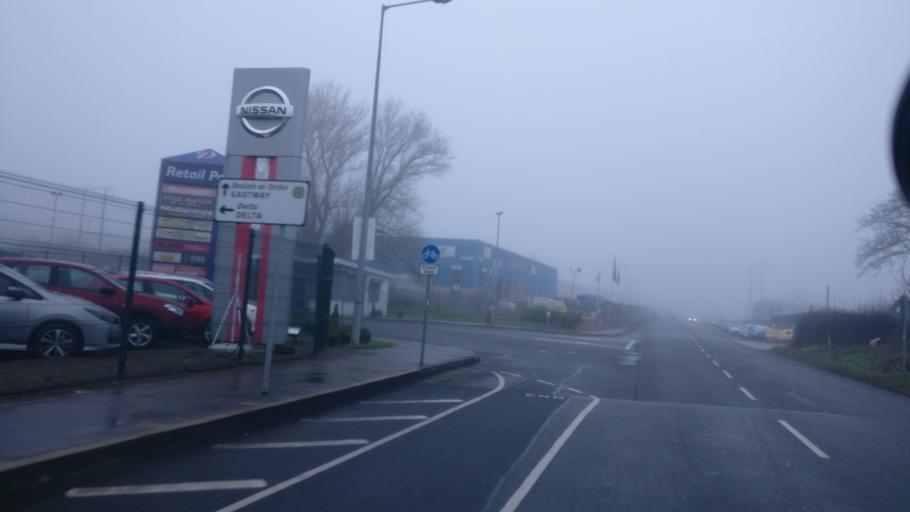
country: IE
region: Munster
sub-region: County Limerick
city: Annacotty
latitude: 52.6489
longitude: -8.5816
